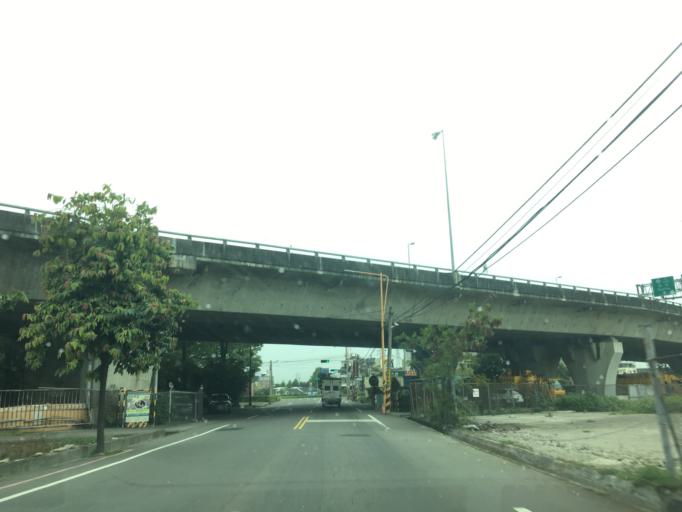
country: TW
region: Taiwan
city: Zhongxing New Village
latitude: 24.0518
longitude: 120.6851
